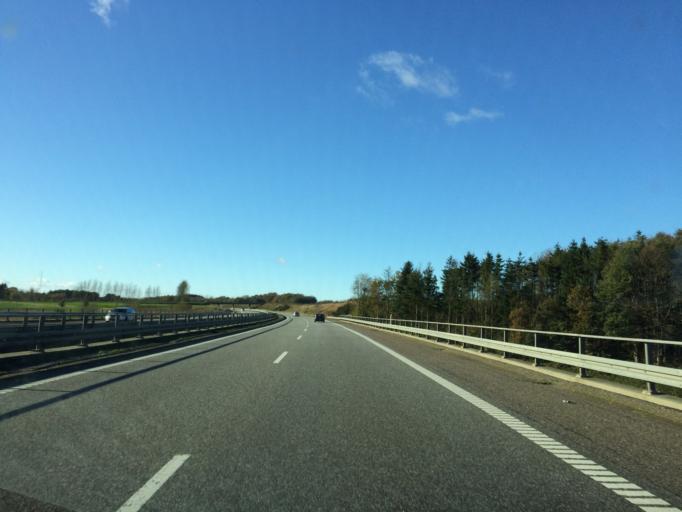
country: DK
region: Central Jutland
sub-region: Hedensted Kommune
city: Torring
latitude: 55.8366
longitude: 9.4489
